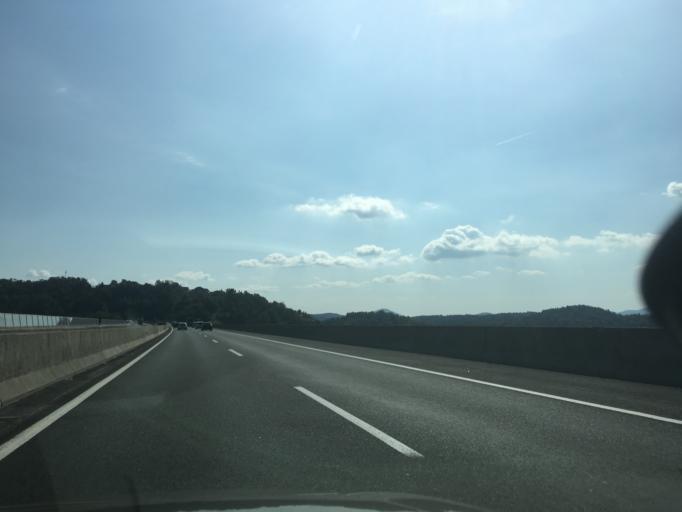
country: SI
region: Skofljica
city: Skofljica
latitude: 45.9908
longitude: 14.5929
